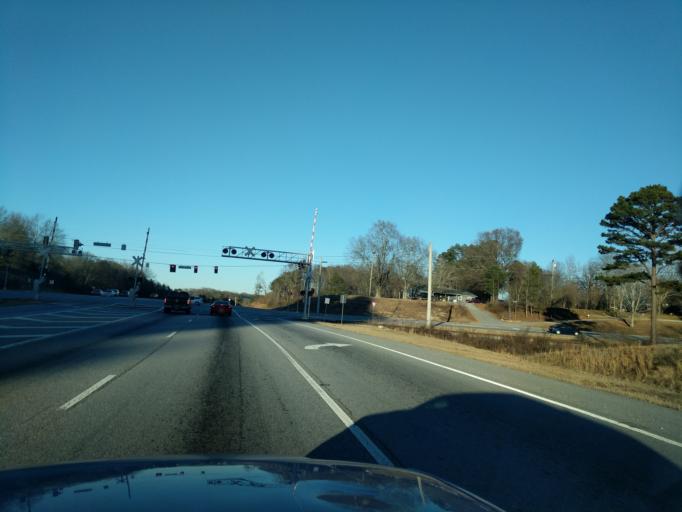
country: US
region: Georgia
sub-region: Stephens County
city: Toccoa
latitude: 34.5349
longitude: -83.2988
